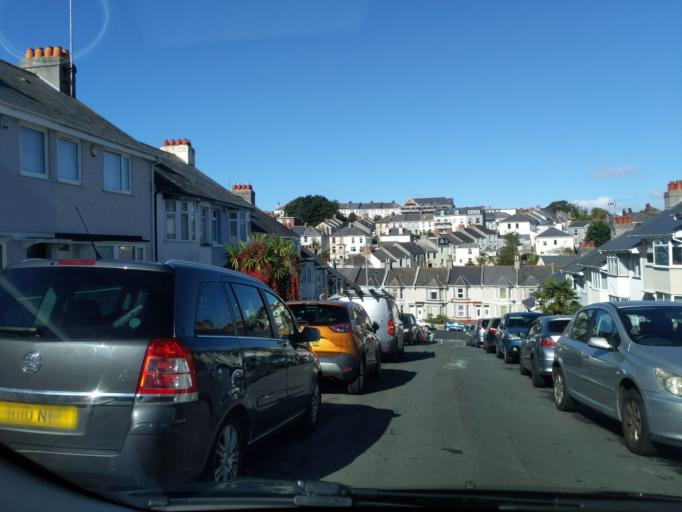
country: GB
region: England
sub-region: Cornwall
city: Millbrook
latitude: 50.3847
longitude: -4.1658
